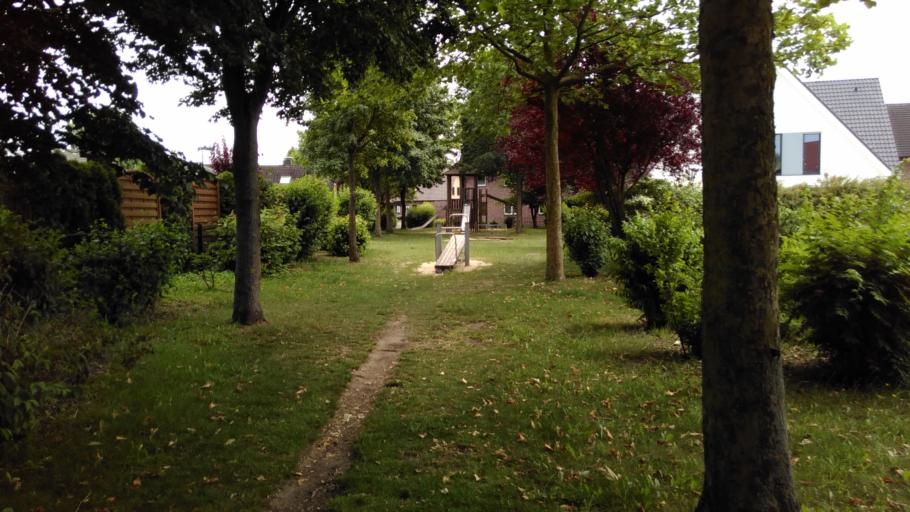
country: DE
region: North Rhine-Westphalia
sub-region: Regierungsbezirk Detmold
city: Verl
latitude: 51.8744
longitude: 8.4982
